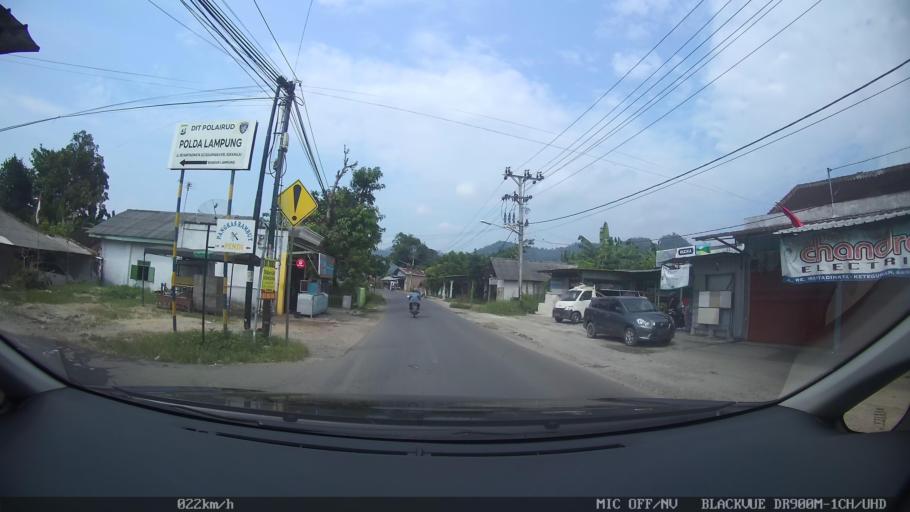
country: ID
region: Lampung
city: Bandarlampung
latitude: -5.4613
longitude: 105.2504
